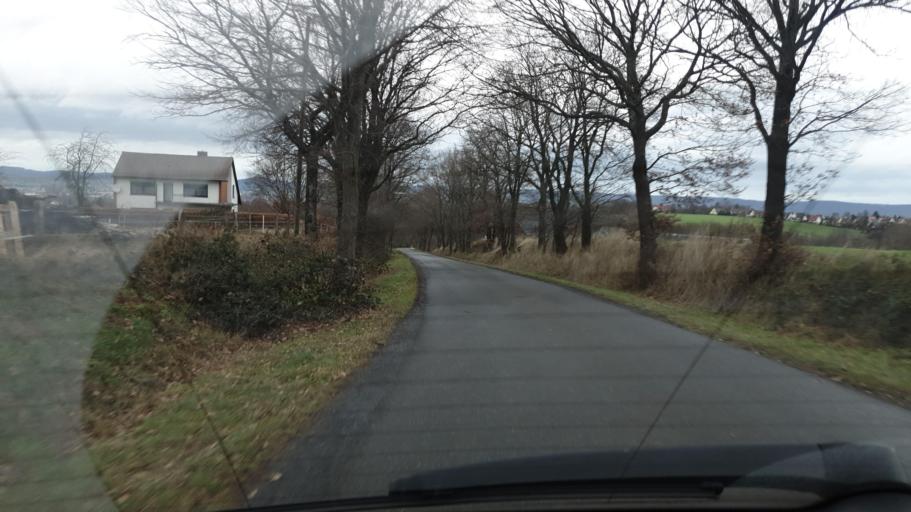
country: DE
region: North Rhine-Westphalia
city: Bad Oeynhausen
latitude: 52.1726
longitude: 8.7854
